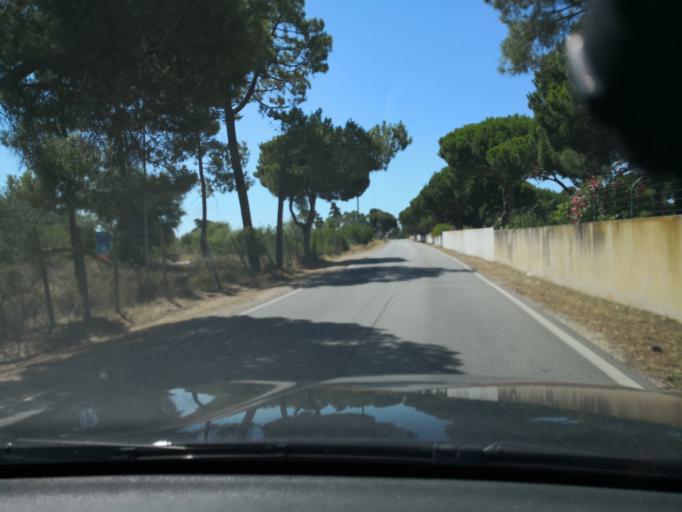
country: PT
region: Faro
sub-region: Loule
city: Vilamoura
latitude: 37.0830
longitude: -8.1002
